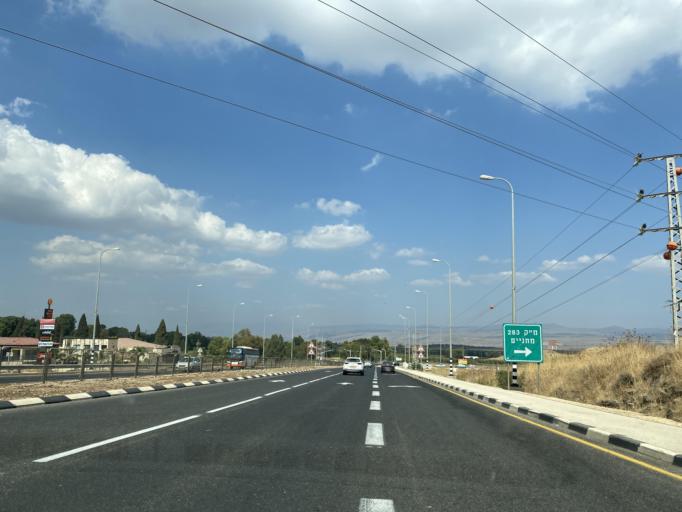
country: IL
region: Northern District
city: Rosh Pinna
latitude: 32.9685
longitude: 35.5515
